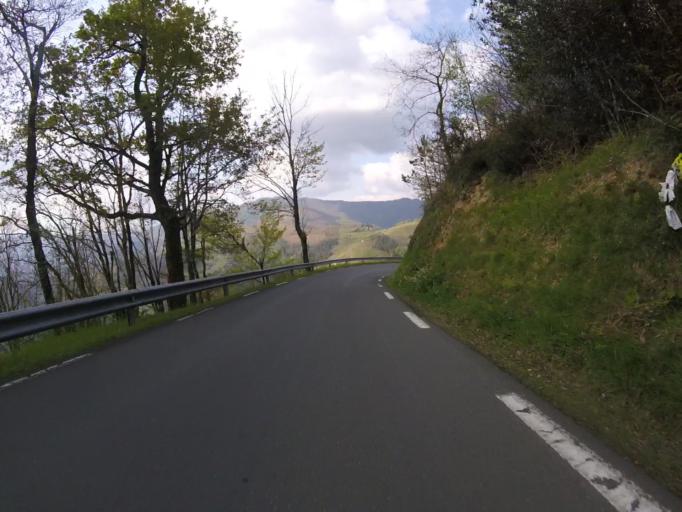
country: ES
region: Basque Country
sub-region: Provincia de Guipuzcoa
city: Azkoitia
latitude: 43.2053
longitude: -2.3536
